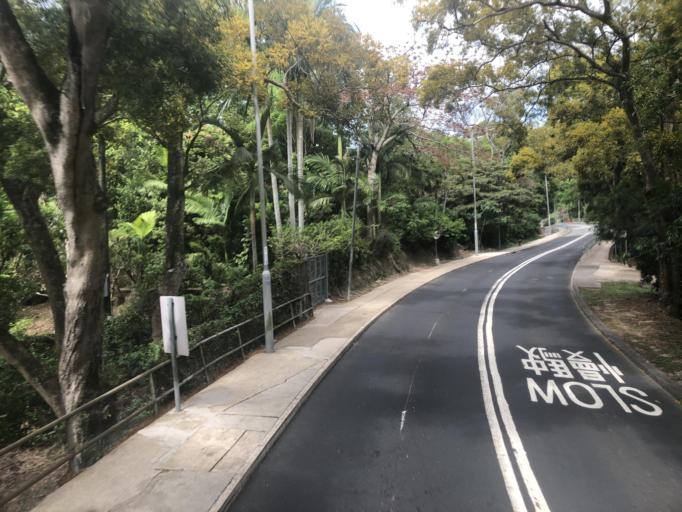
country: HK
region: Sai Kung
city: Sai Kung
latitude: 22.3910
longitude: 114.2954
